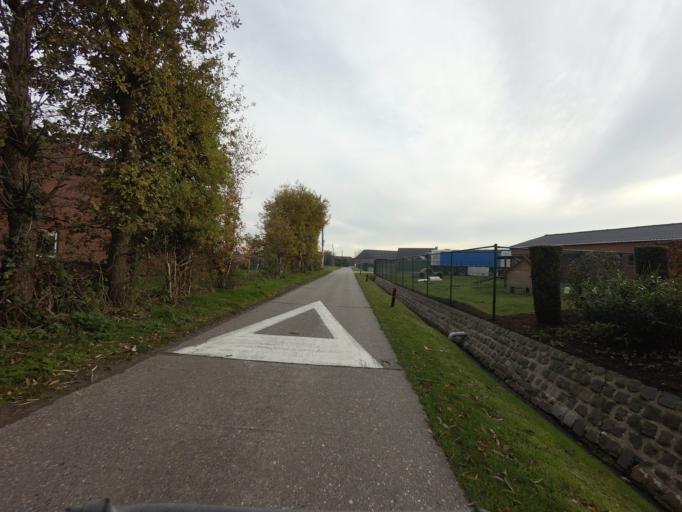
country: BE
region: Flanders
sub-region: Provincie Antwerpen
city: Hoogstraten
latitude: 51.4540
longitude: 4.7518
